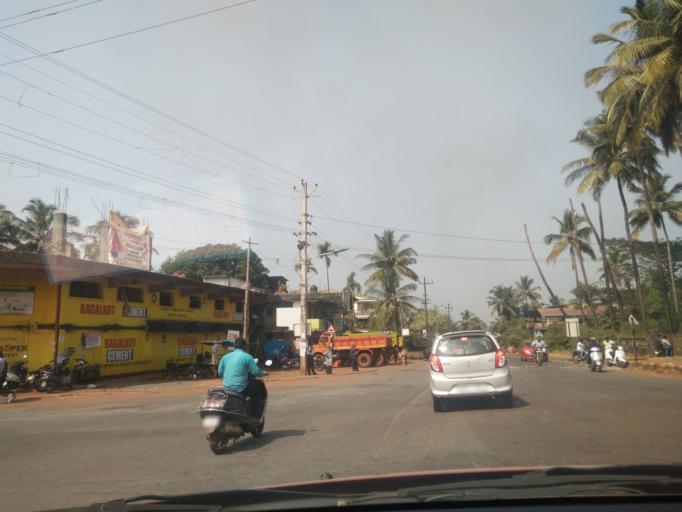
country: IN
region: Goa
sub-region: North Goa
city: Sanquelim
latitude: 15.5575
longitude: 74.0159
